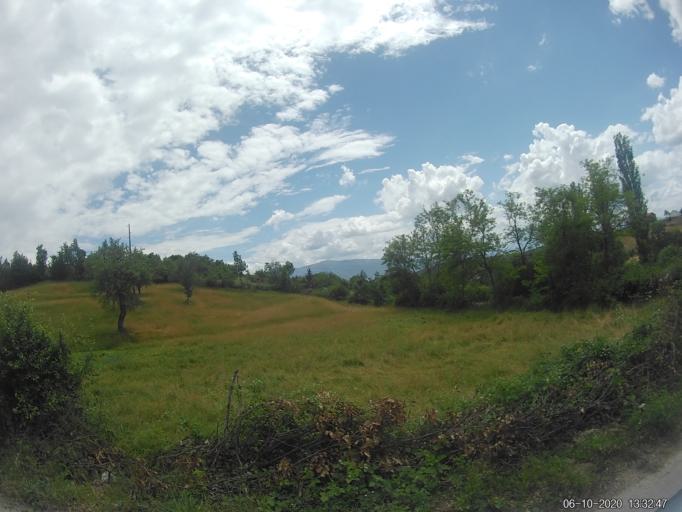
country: XK
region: Prizren
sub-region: Komuna e Therandes
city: Peqan
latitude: 42.4109
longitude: 20.8840
